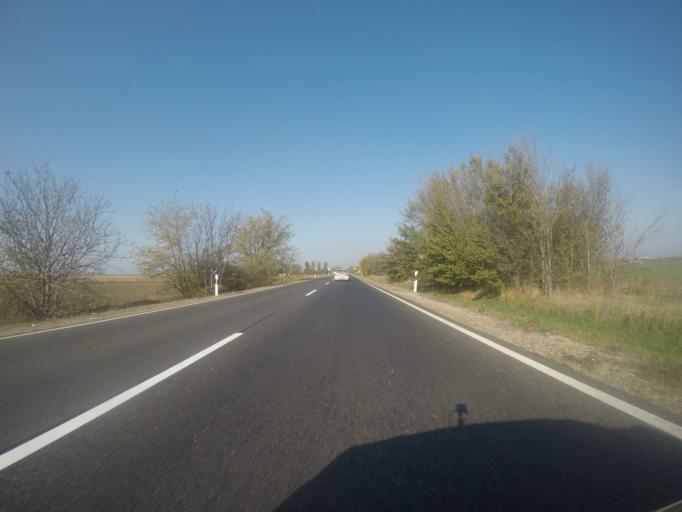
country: HU
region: Fejer
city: Baracs
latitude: 46.8918
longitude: 18.9209
